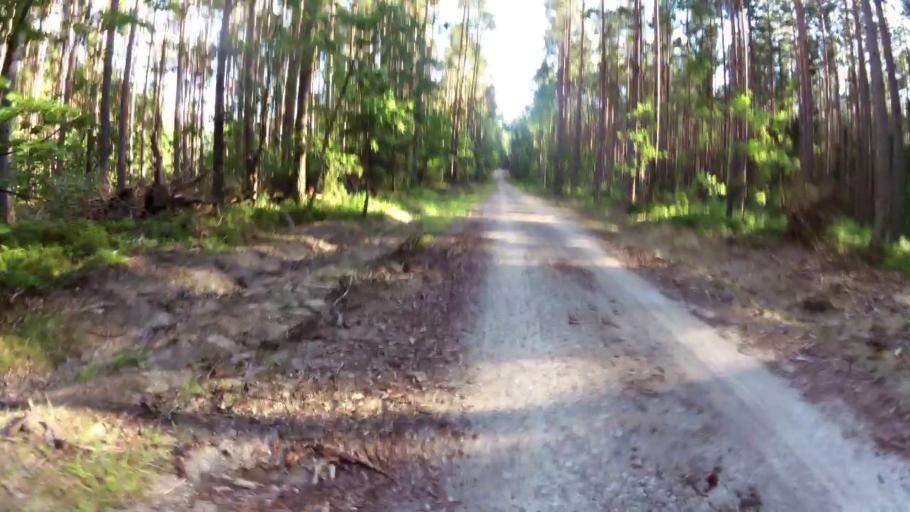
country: PL
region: West Pomeranian Voivodeship
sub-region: Powiat bialogardzki
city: Bialogard
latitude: 53.9591
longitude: 16.0959
